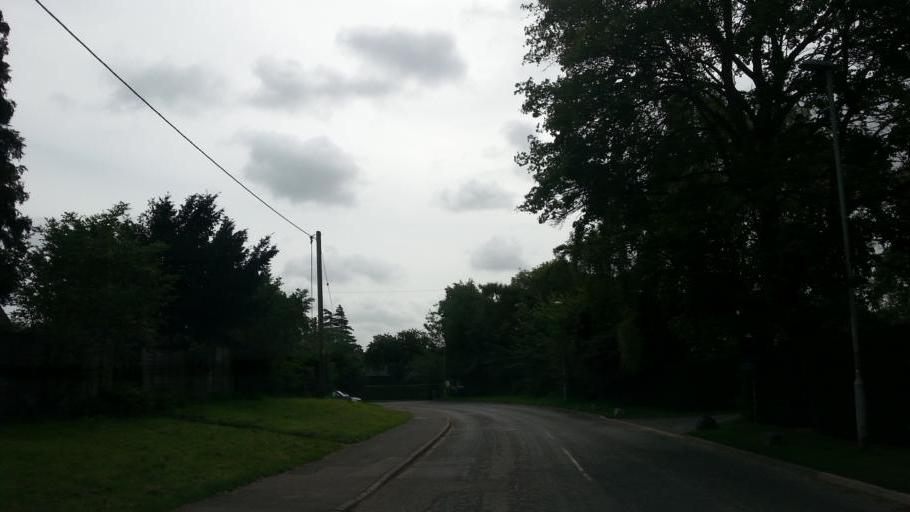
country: GB
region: England
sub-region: Cambridgeshire
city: Barton
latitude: 52.1844
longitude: 0.0515
